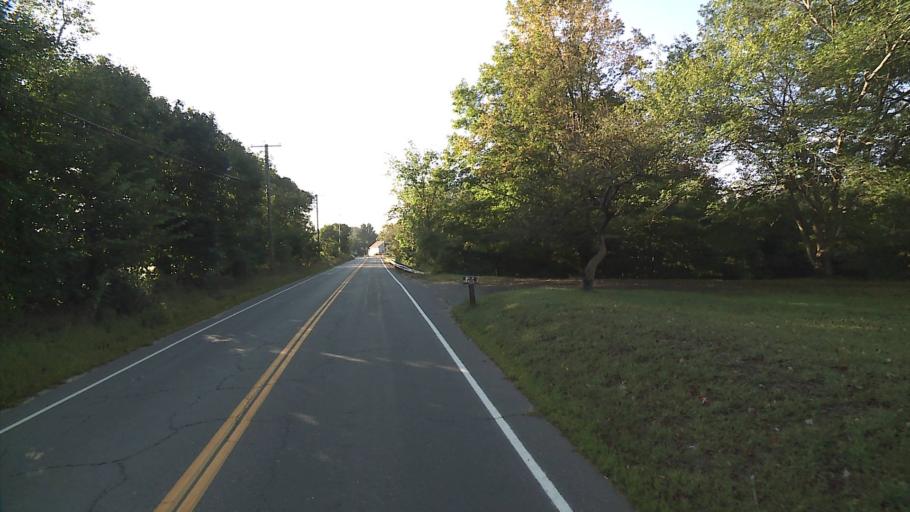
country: US
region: Connecticut
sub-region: Tolland County
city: South Coventry
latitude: 41.7944
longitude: -72.2859
